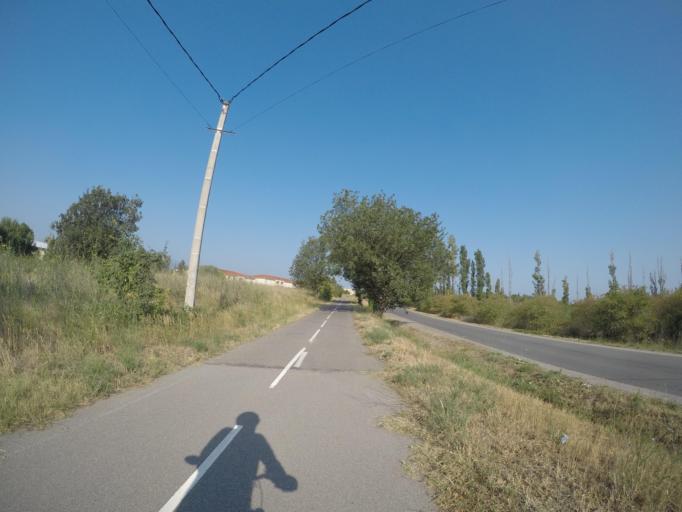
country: FR
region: Languedoc-Roussillon
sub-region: Departement des Pyrenees-Orientales
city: Llupia
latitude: 42.6221
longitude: 2.7753
